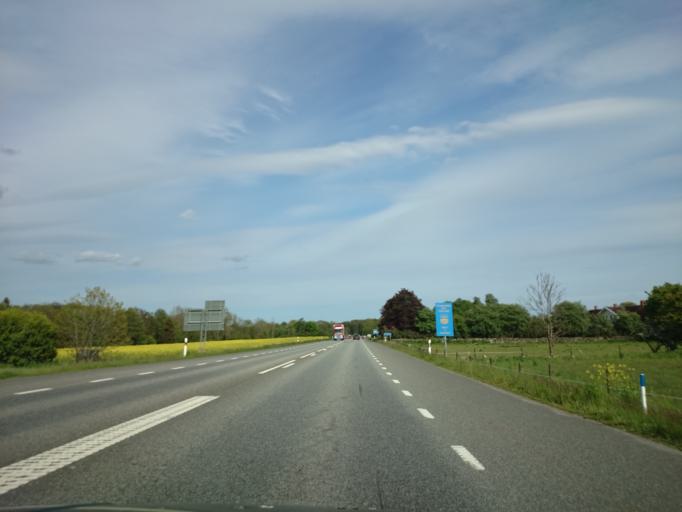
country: SE
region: Skane
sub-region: Kristianstads Kommun
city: Onnestad
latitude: 55.9298
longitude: 13.9582
